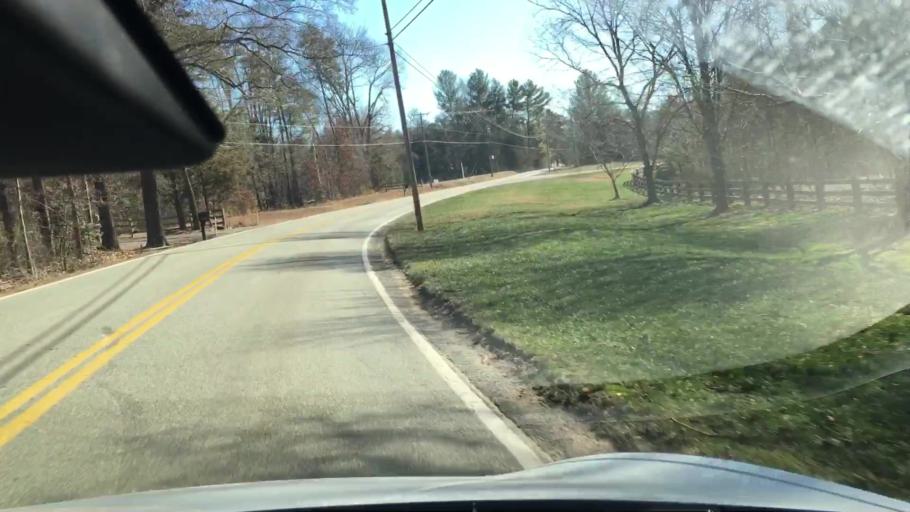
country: US
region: Virginia
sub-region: Goochland County
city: Goochland
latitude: 37.5916
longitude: -77.7592
